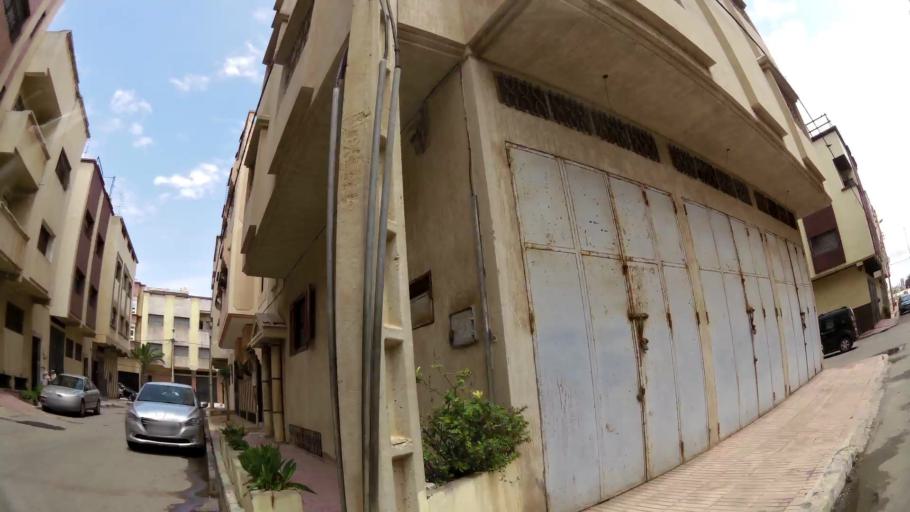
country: MA
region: Rabat-Sale-Zemmour-Zaer
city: Sale
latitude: 34.0473
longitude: -6.8201
